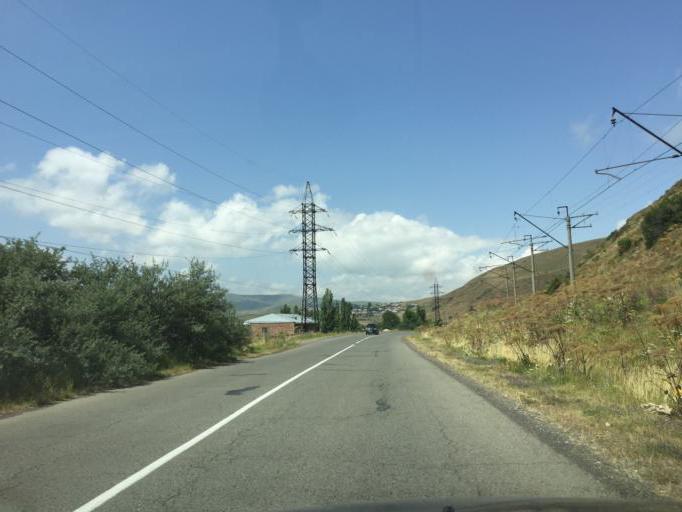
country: AM
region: Geghark'unik'i Marz
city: Tsovagyugh
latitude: 40.6308
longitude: 44.9952
